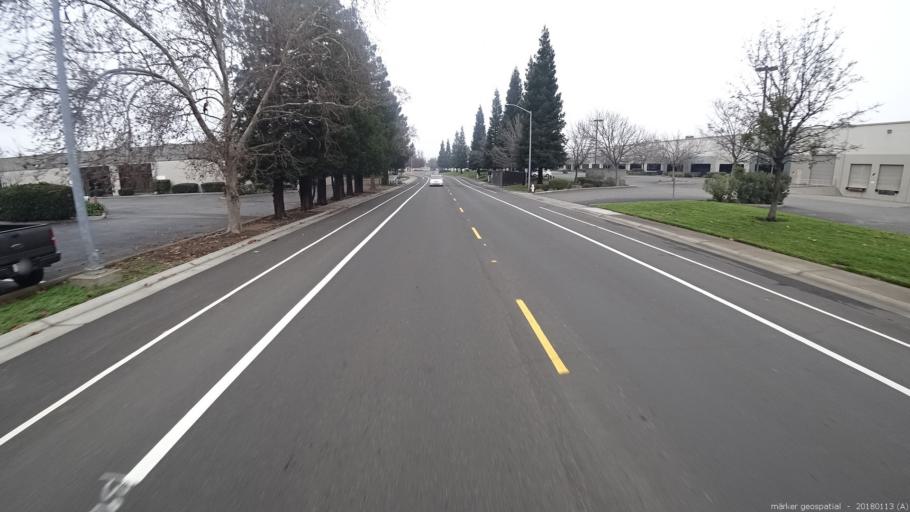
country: US
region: California
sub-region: Sacramento County
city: Gold River
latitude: 38.6002
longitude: -121.2612
